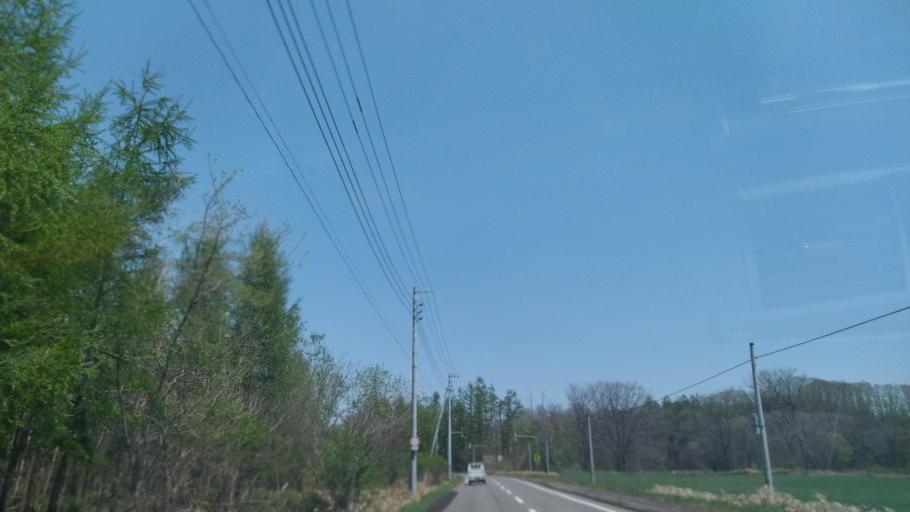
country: JP
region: Hokkaido
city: Obihiro
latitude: 42.8239
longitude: 142.9879
